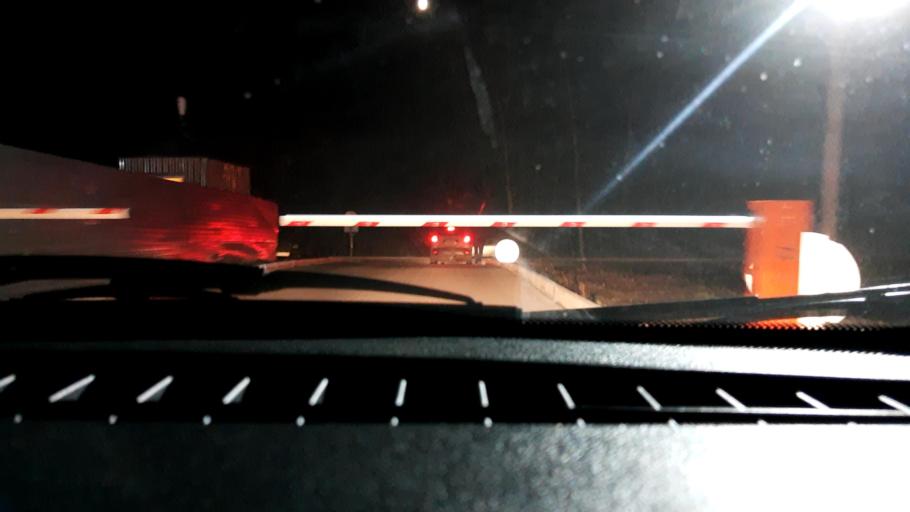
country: RU
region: Bashkortostan
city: Ufa
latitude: 54.7955
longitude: 55.9590
